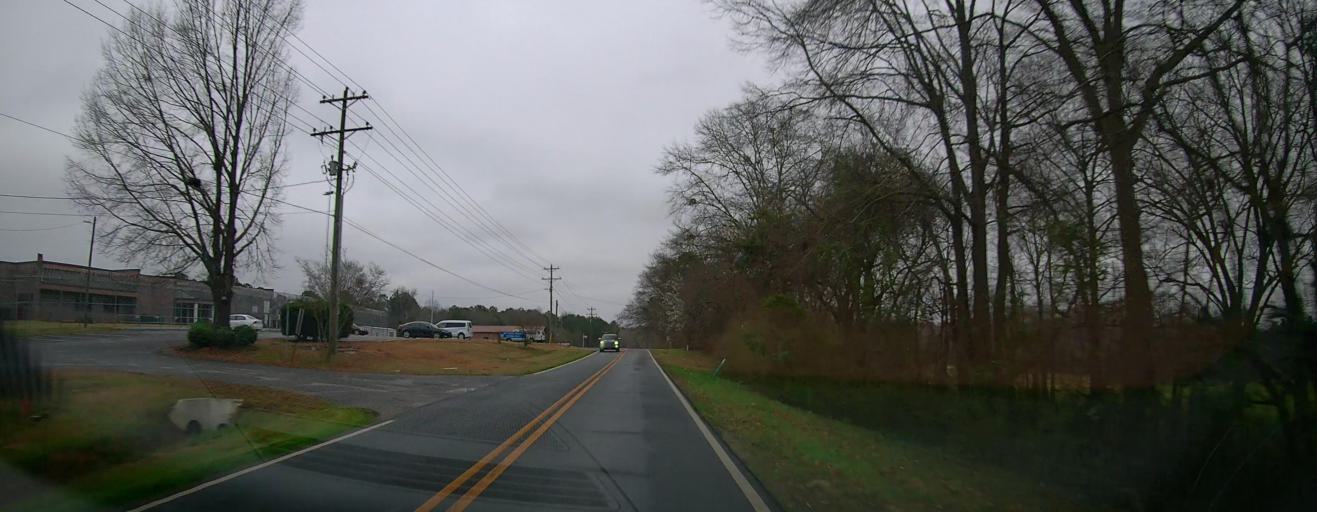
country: US
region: Georgia
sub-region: Pike County
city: Zebulon
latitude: 33.1152
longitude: -84.3612
